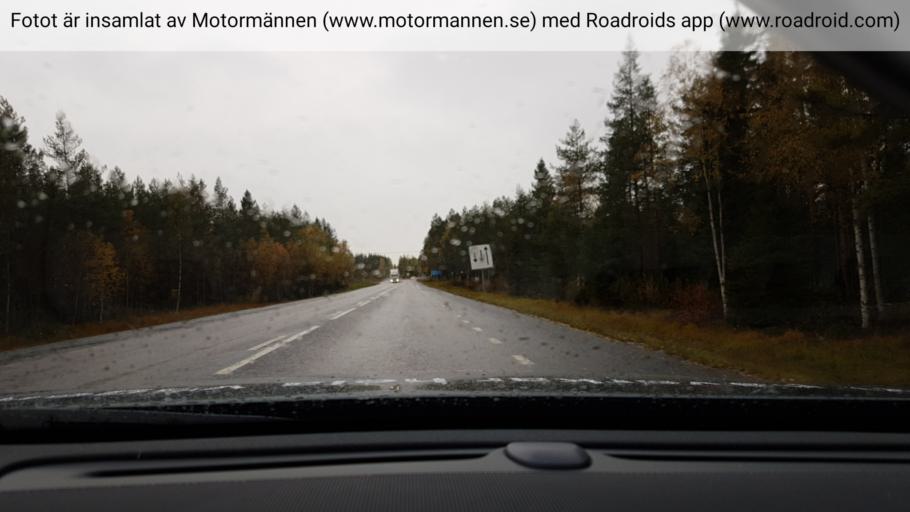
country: SE
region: Norrbotten
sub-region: Lulea Kommun
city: Gammelstad
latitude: 65.5821
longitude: 22.0064
